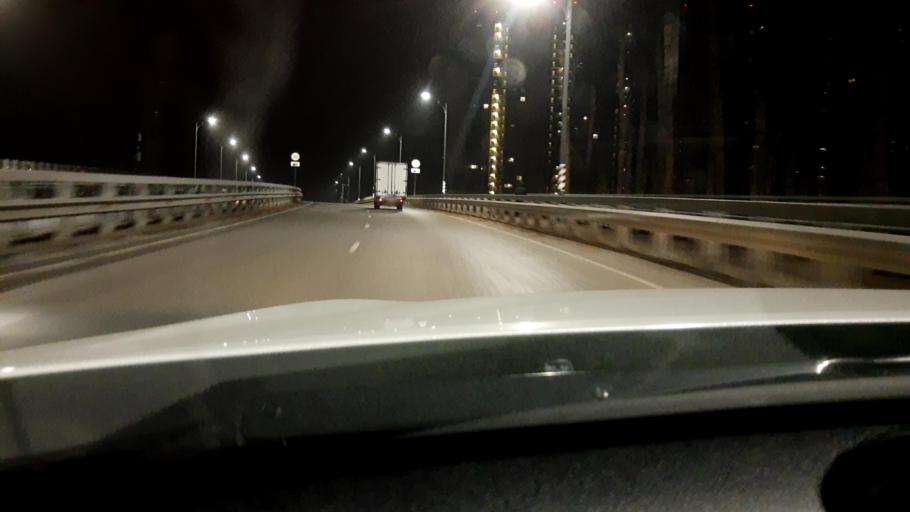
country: RU
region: Moskovskaya
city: Reutov
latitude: 55.7586
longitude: 37.8841
